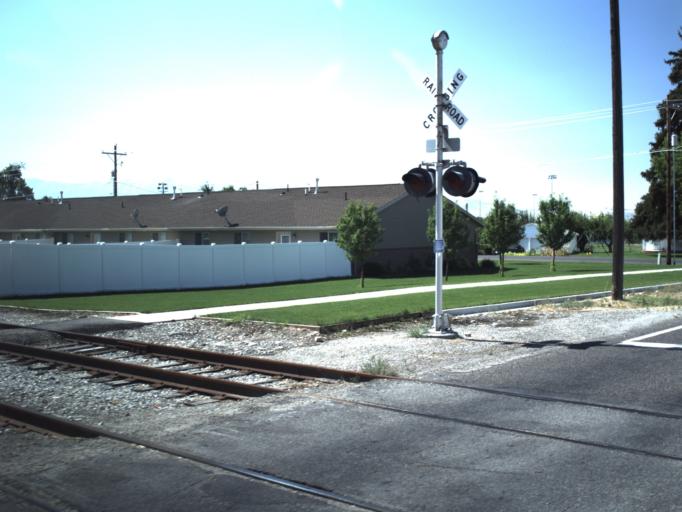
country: US
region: Utah
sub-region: Cache County
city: Smithfield
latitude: 41.8387
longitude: -111.8430
